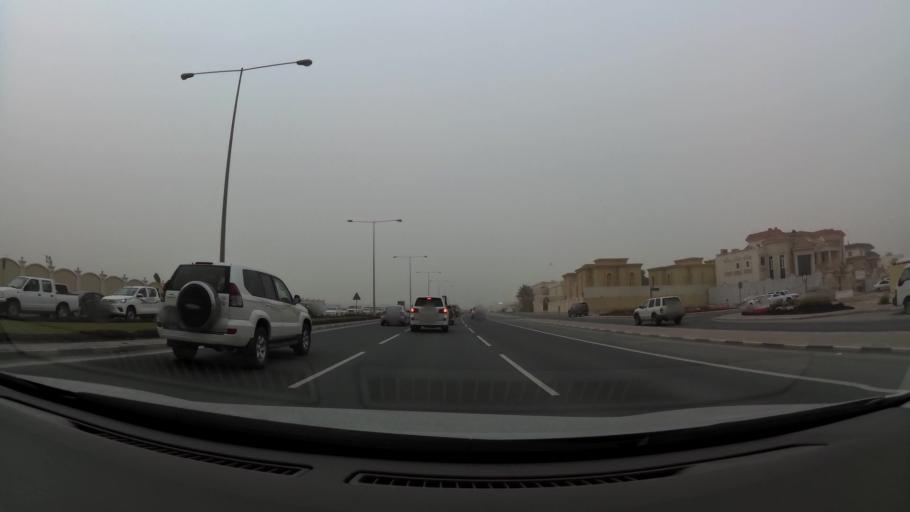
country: QA
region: Baladiyat ad Dawhah
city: Doha
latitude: 25.2404
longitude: 51.4964
